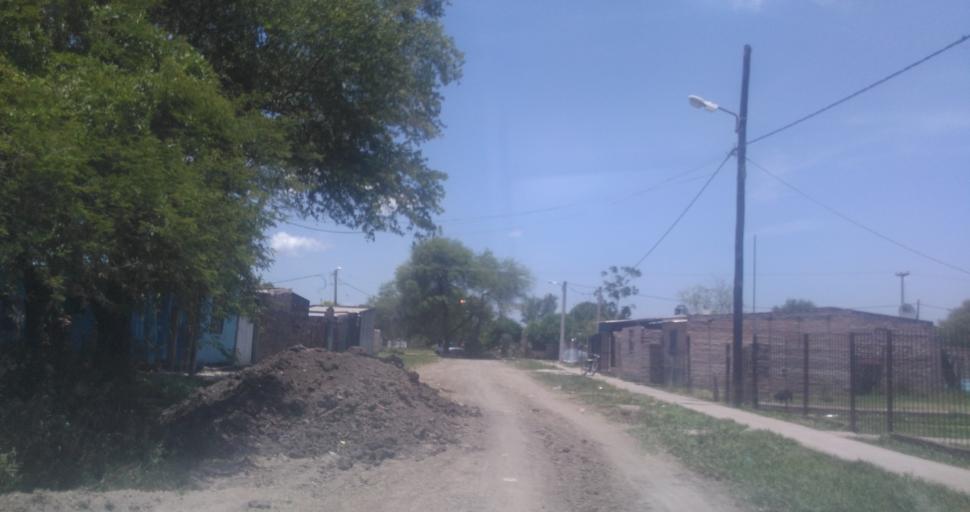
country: AR
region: Chaco
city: Fontana
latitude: -27.4235
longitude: -59.0391
